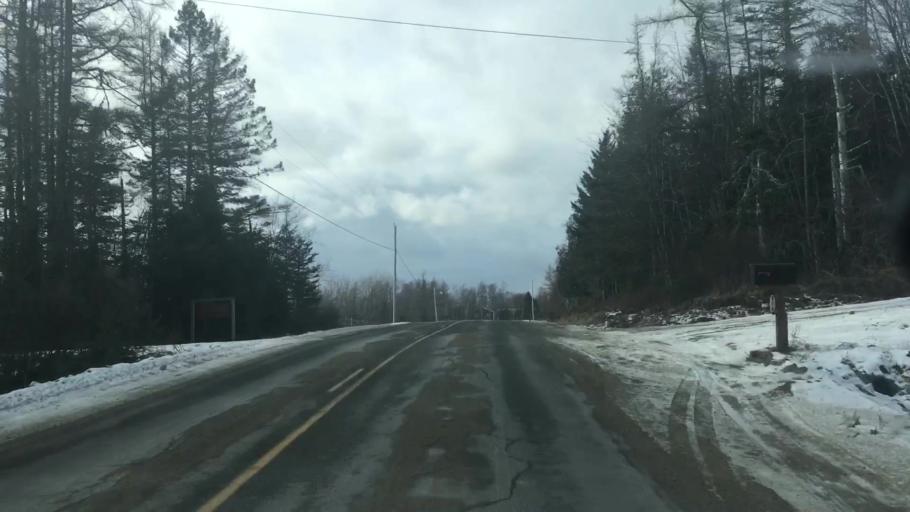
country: US
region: Maine
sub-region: Washington County
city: Machias
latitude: 44.6561
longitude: -67.5279
